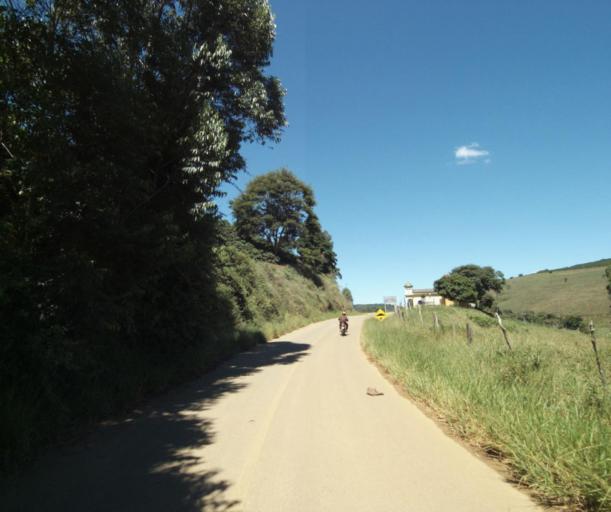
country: BR
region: Minas Gerais
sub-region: Espera Feliz
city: Espera Feliz
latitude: -20.5929
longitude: -41.8384
